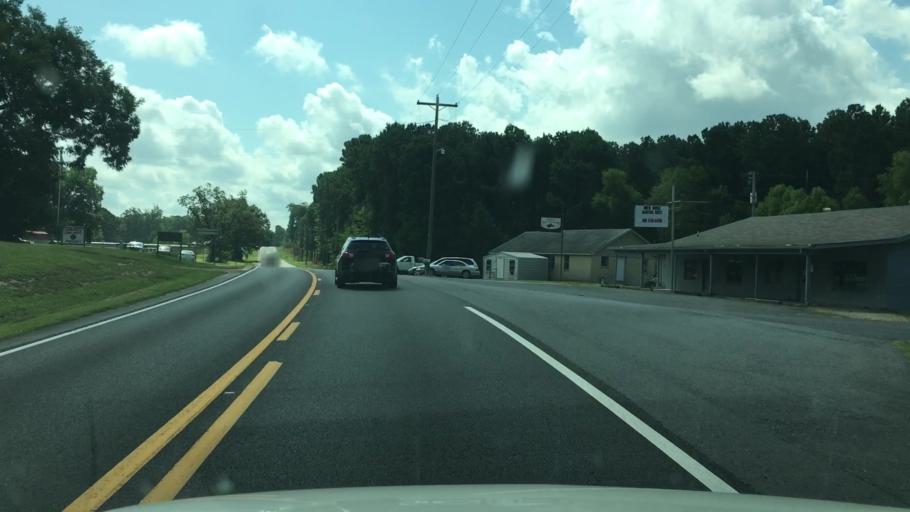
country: US
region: Arkansas
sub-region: Garland County
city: Lake Hamilton
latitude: 34.2685
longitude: -93.1438
